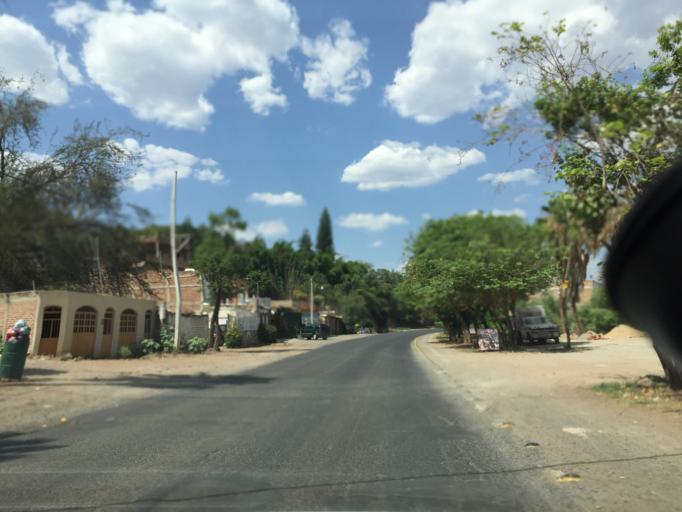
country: MX
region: Jalisco
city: Atotonilco el Alto
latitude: 20.5564
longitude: -102.4932
